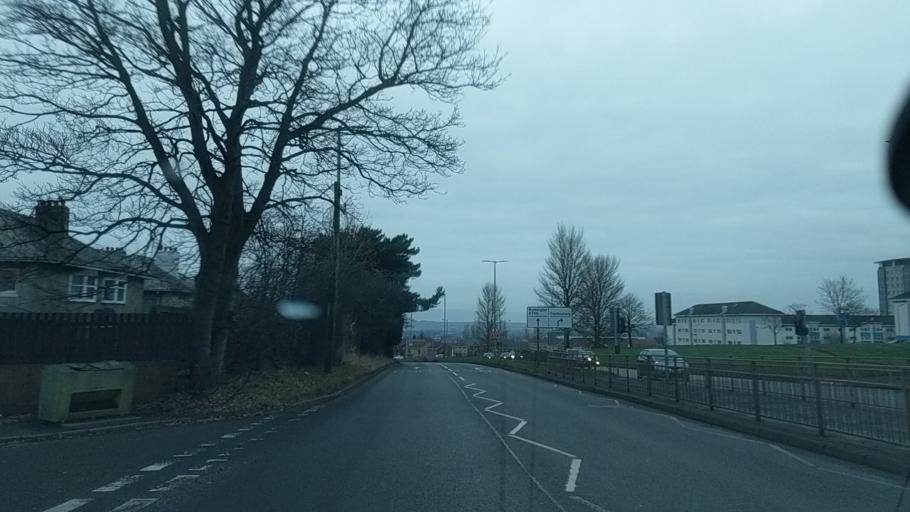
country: GB
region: Scotland
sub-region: South Lanarkshire
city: Rutherglen
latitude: 55.8072
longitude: -4.1844
